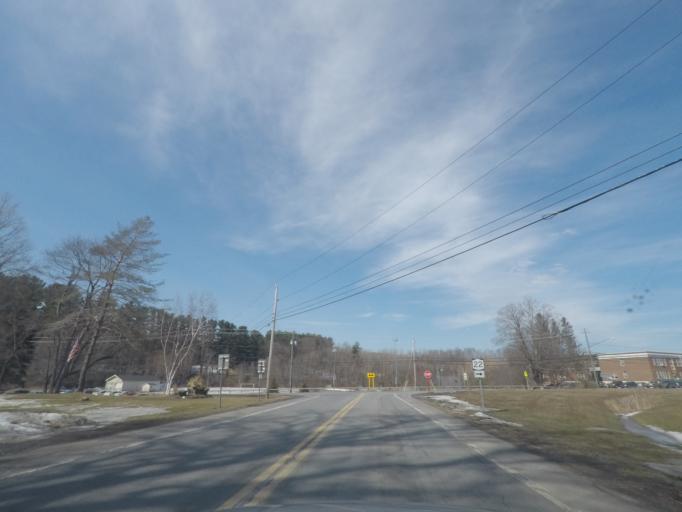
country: US
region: Massachusetts
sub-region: Berkshire County
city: Richmond
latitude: 42.4735
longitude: -73.3812
